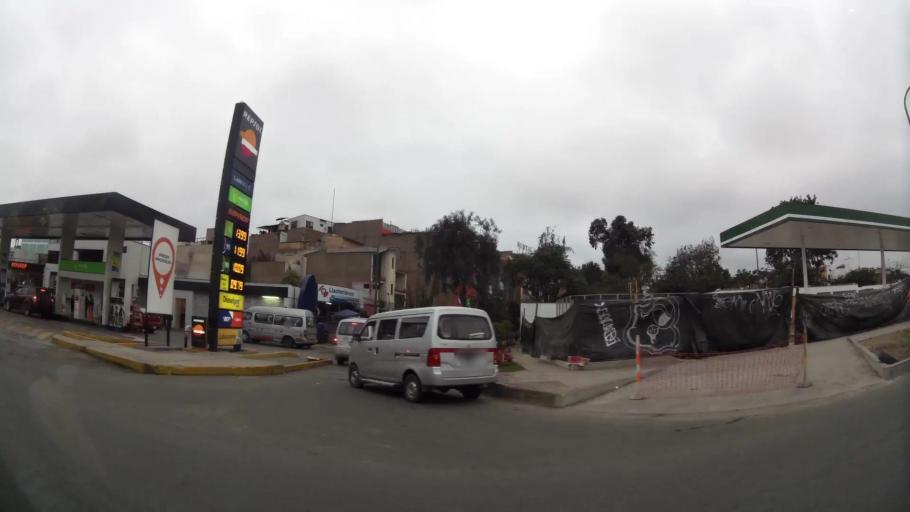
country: PE
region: Lima
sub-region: Lima
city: San Luis
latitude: -12.0770
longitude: -76.9759
